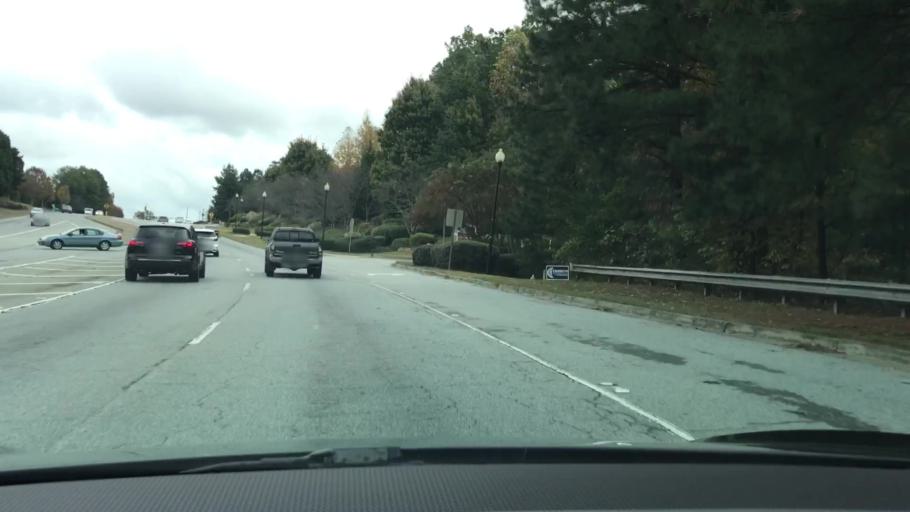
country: US
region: Georgia
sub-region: Gwinnett County
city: Suwanee
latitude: 34.0465
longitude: -84.0889
